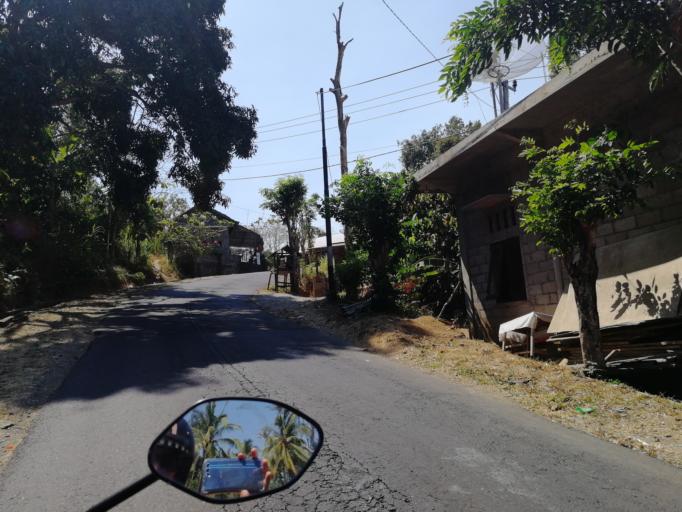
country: ID
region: Bali
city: Banjar Kedisan
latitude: -8.1430
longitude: 115.3110
